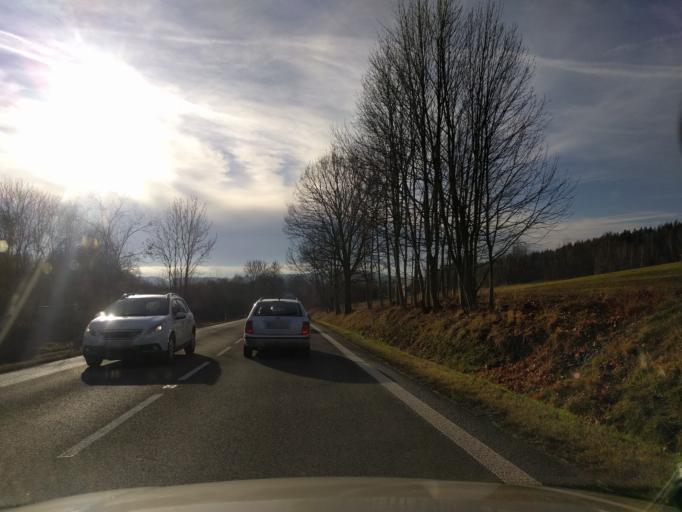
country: CZ
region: Liberecky
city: Mnisek
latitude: 50.8537
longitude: 15.0315
